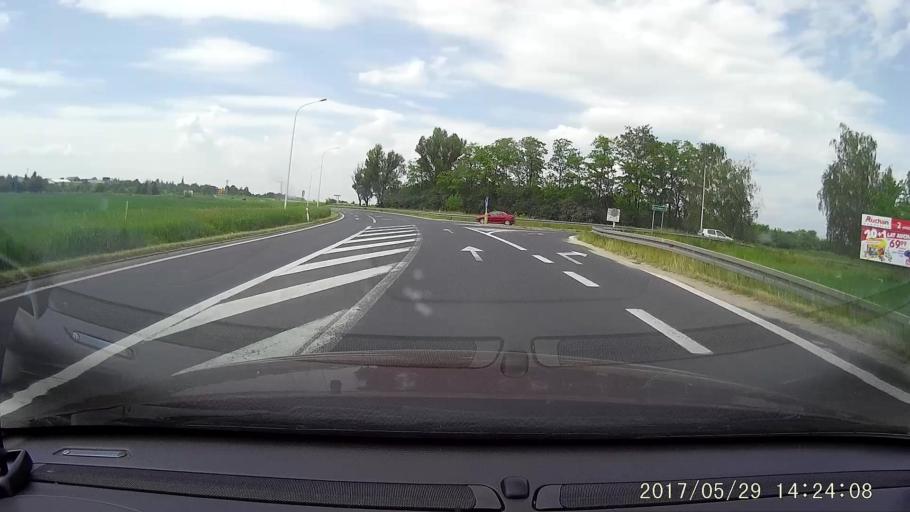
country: PL
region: Lower Silesian Voivodeship
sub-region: Powiat zgorzelecki
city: Lagow
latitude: 51.1445
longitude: 15.0349
